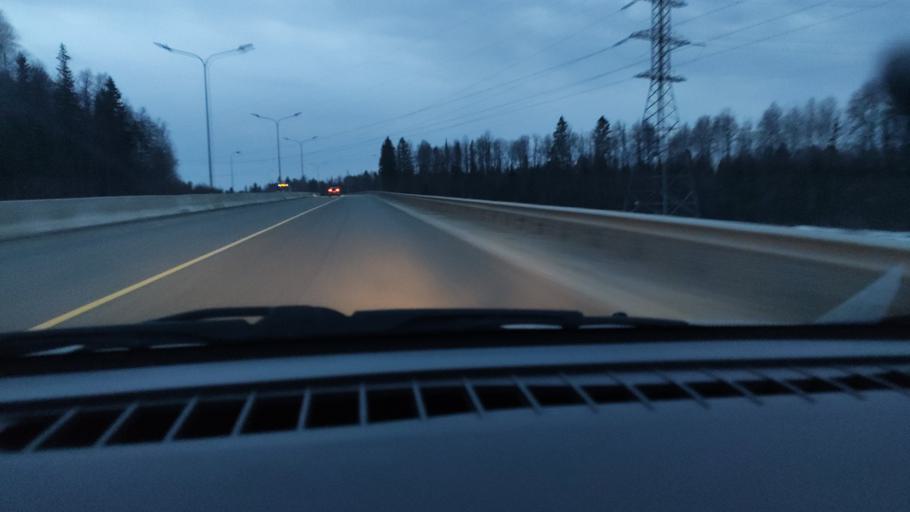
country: RU
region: Perm
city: Novyye Lyady
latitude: 58.0661
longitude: 56.4290
